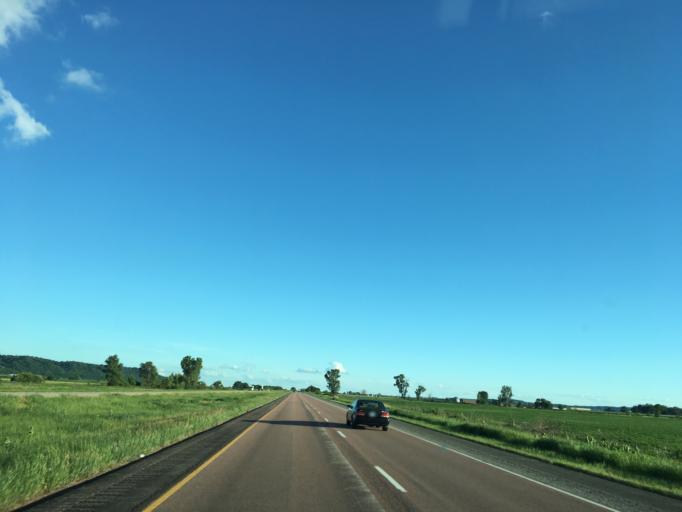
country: US
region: Nebraska
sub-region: Cass County
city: Plattsmouth
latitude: 40.9774
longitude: -95.8003
